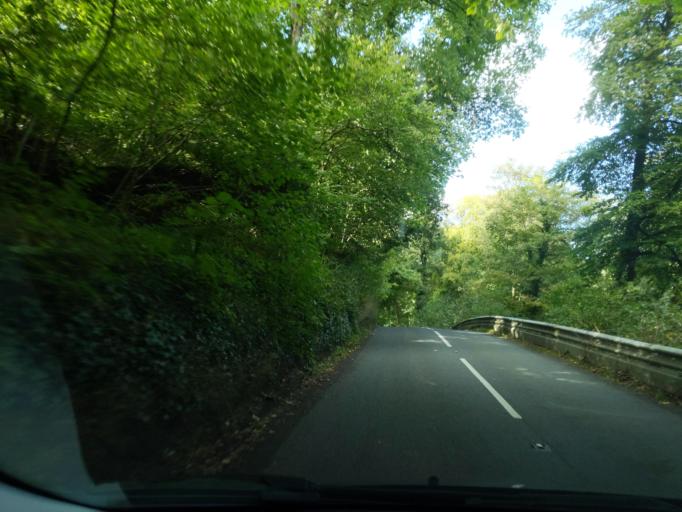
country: GB
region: England
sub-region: Devon
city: Chudleigh
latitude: 50.6226
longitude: -3.6348
